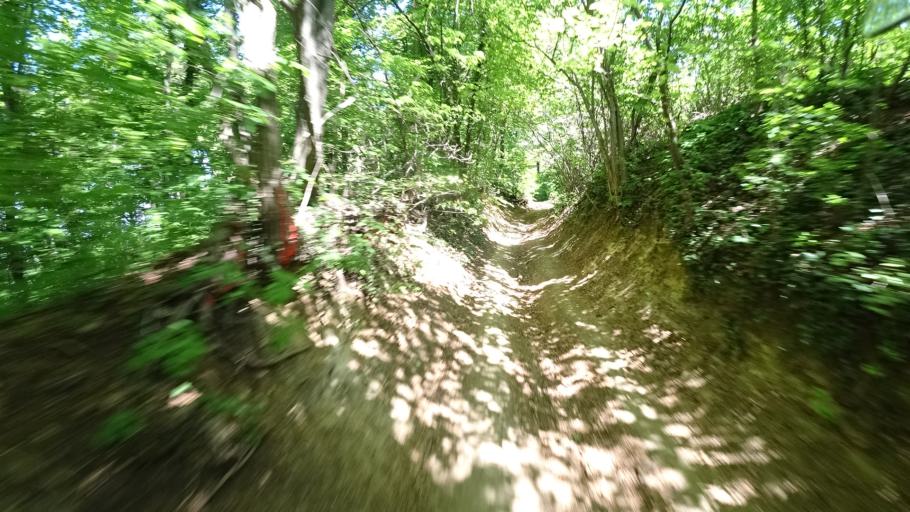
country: HR
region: Zagrebacka
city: Bestovje
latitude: 45.8332
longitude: 15.8336
